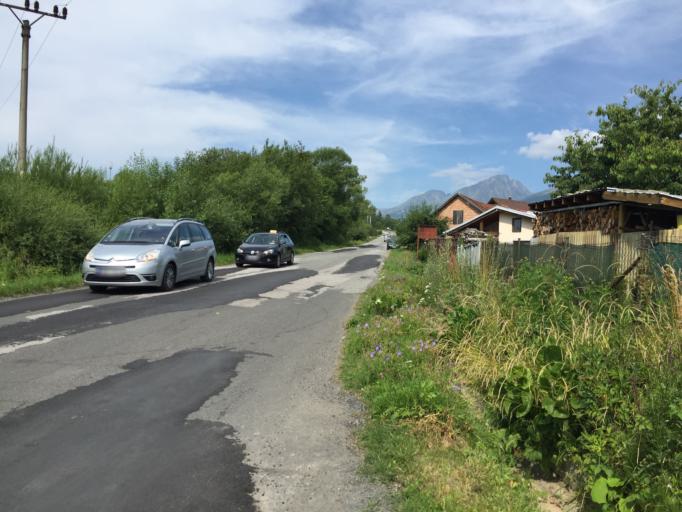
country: SK
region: Presovsky
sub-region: Okres Poprad
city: Nova Lesna
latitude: 49.1227
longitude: 20.2633
